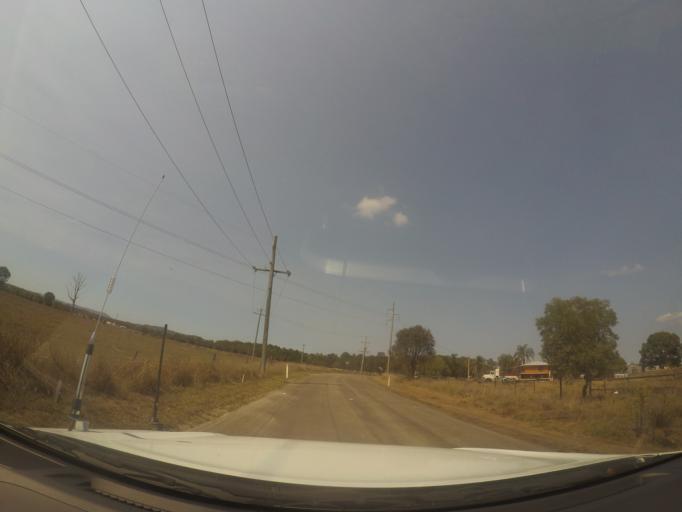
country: AU
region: Queensland
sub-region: Logan
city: Chambers Flat
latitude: -27.7659
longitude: 153.0630
